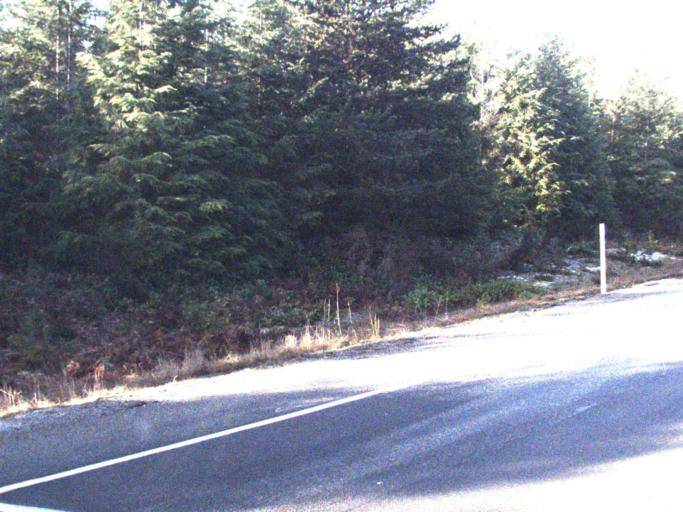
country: US
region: Washington
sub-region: Snohomish County
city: Darrington
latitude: 48.2703
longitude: -121.6435
